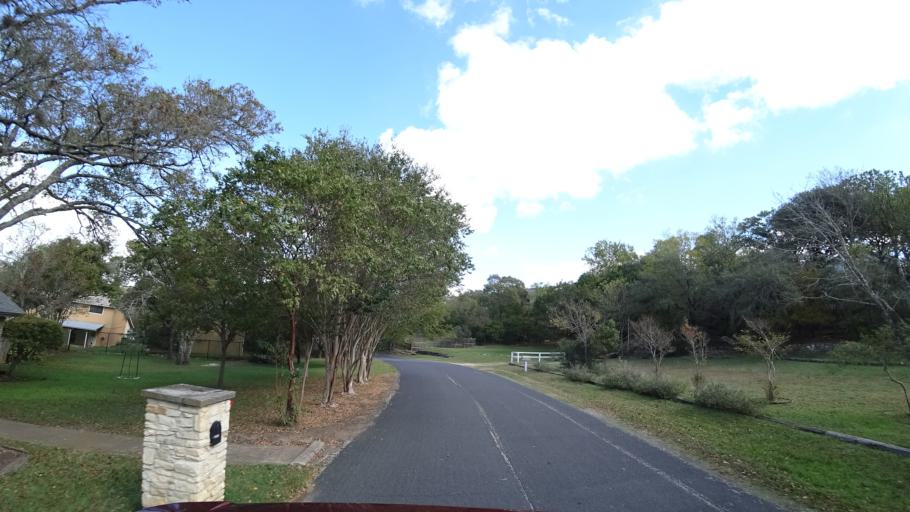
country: US
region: Texas
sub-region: Williamson County
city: Jollyville
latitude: 30.4186
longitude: -97.7844
